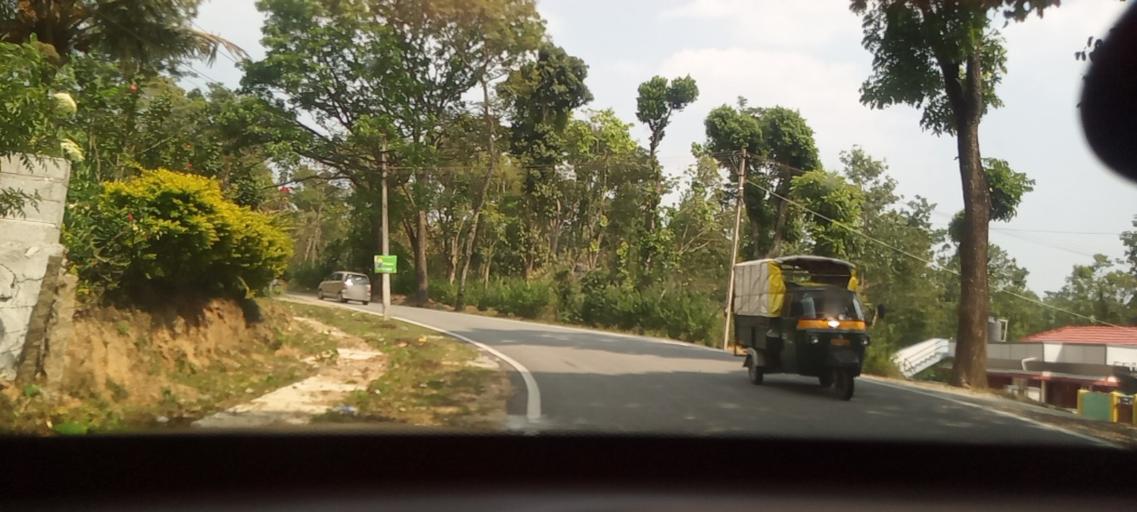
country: IN
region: Karnataka
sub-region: Chikmagalur
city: Chikmagalur
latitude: 13.2623
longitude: 75.6831
